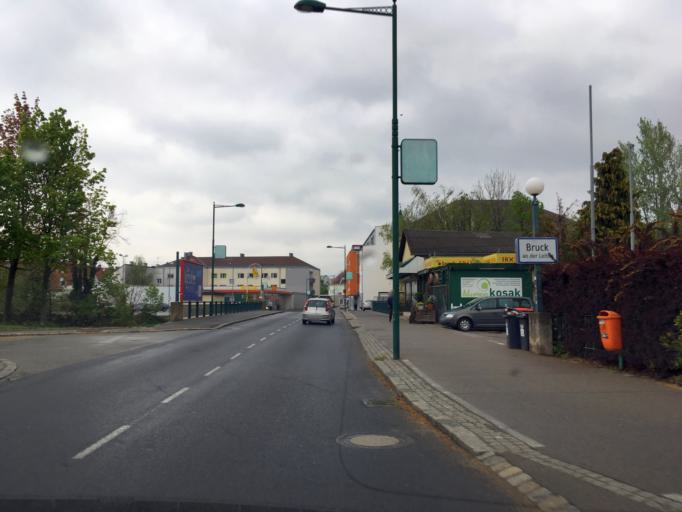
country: AT
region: Burgenland
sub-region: Politischer Bezirk Neusiedl am See
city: Bruckneudorf
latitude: 48.0203
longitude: 16.7778
